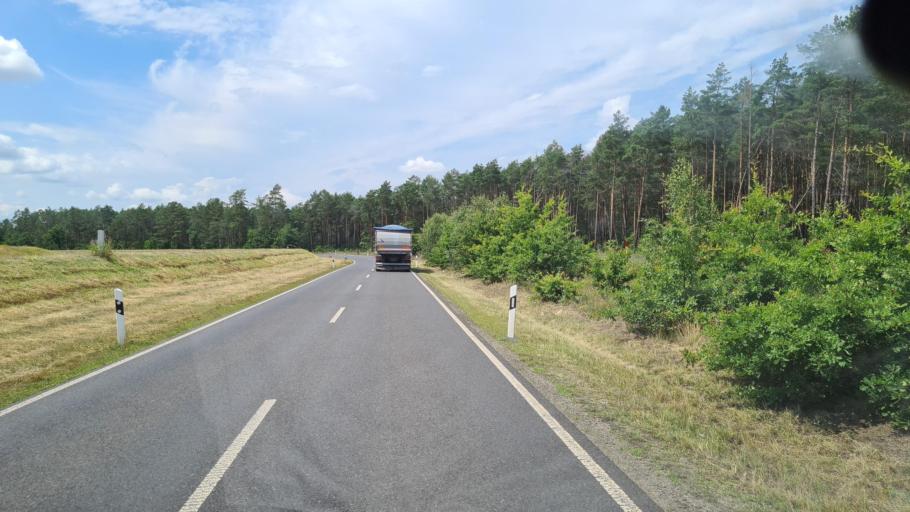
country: DE
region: Brandenburg
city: Welzow
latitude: 51.4932
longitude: 14.1521
